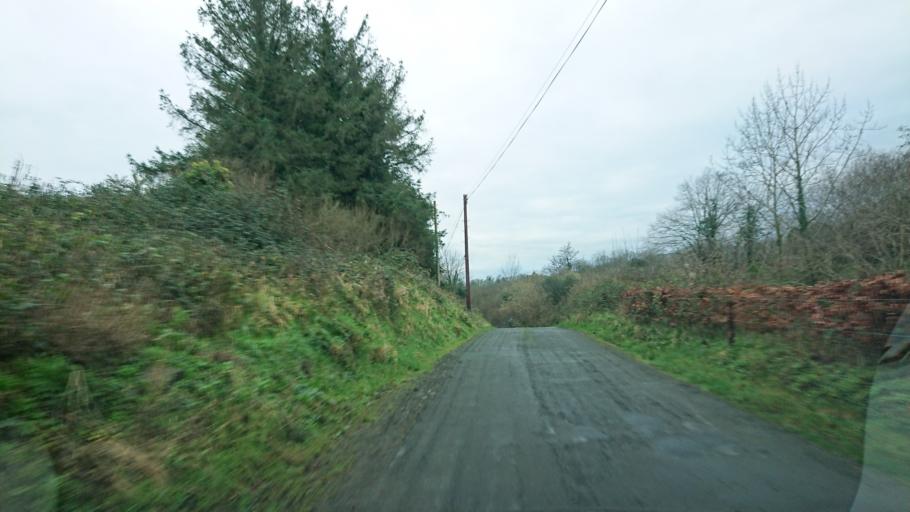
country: IE
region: Leinster
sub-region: Kilkenny
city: Mooncoin
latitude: 52.2309
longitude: -7.2478
